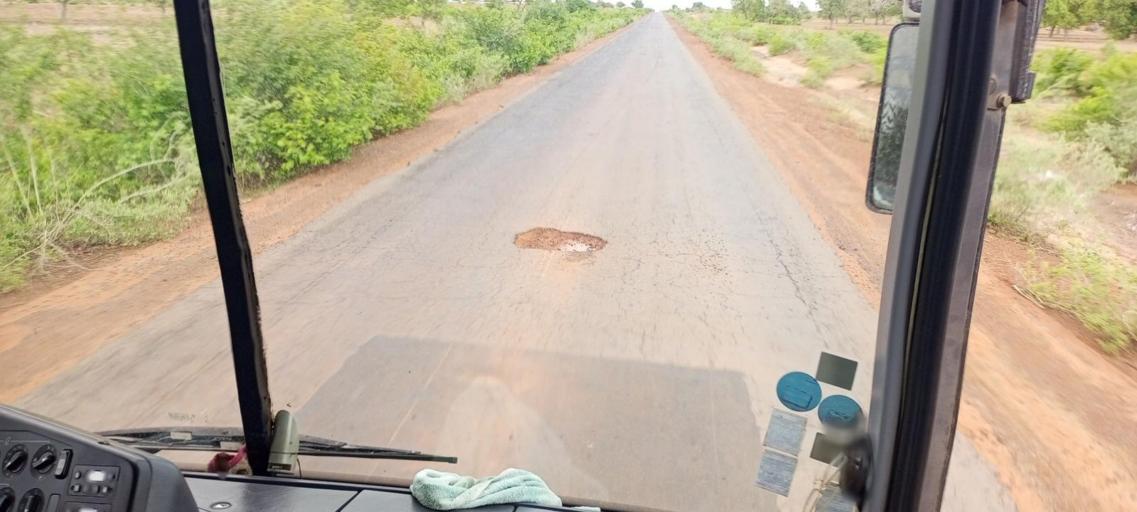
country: ML
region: Segou
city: Bla
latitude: 12.7240
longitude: -5.7251
